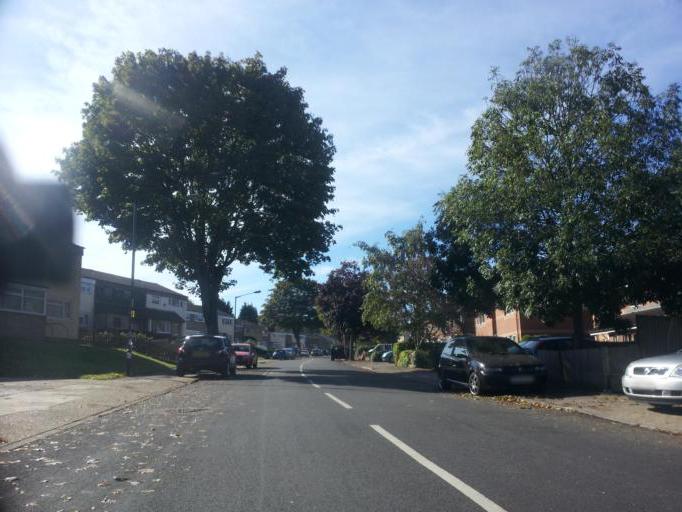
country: GB
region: England
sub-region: Kent
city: Chatham
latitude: 51.3605
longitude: 0.5343
